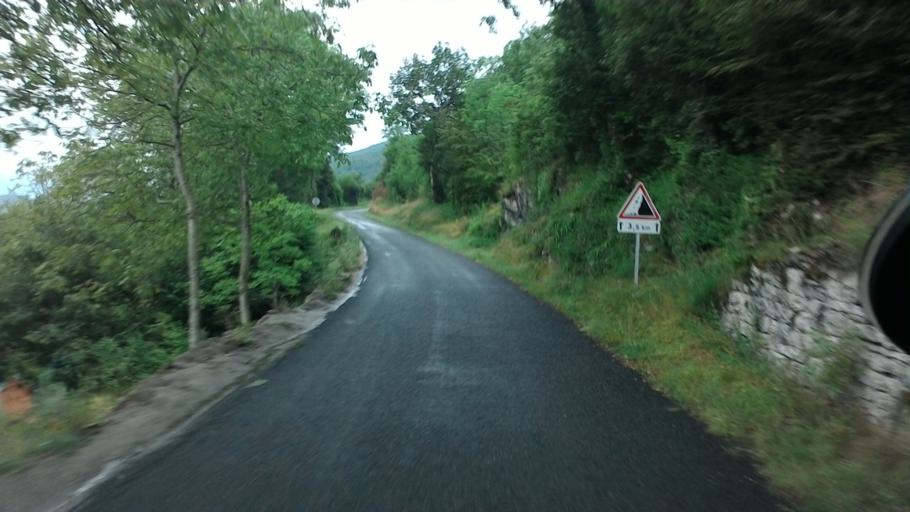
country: FR
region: Rhone-Alpes
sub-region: Departement de l'Ain
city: Belley
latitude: 45.7624
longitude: 5.6049
